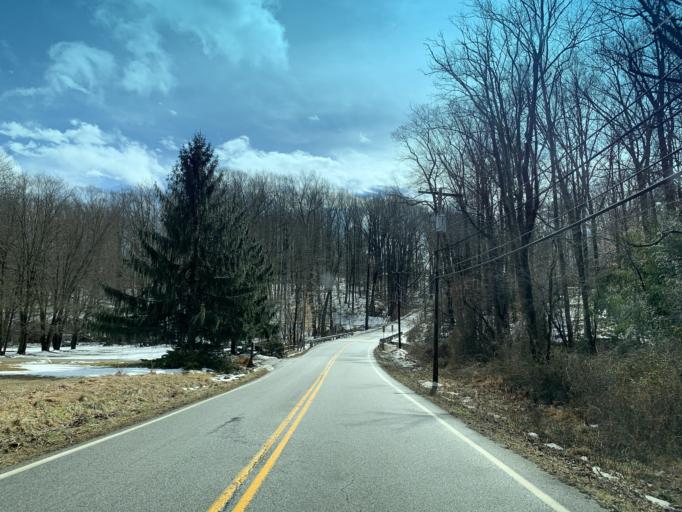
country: US
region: Delaware
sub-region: New Castle County
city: Newark
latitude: 39.7024
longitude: -75.7999
